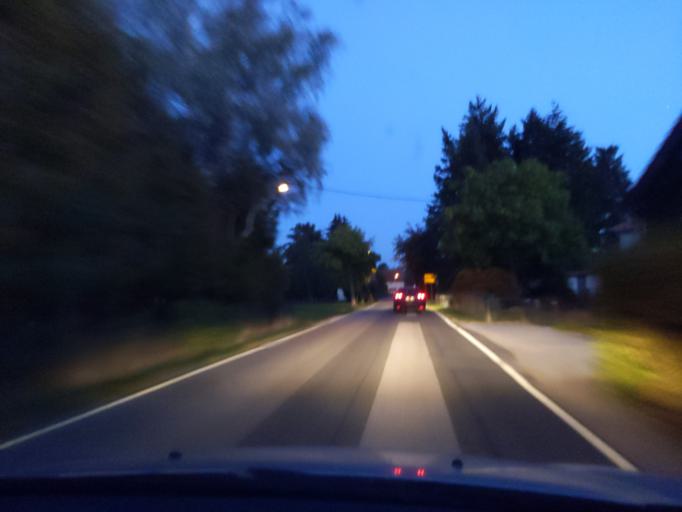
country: DE
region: Saxony
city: Malschwitz
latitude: 51.2672
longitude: 14.5240
